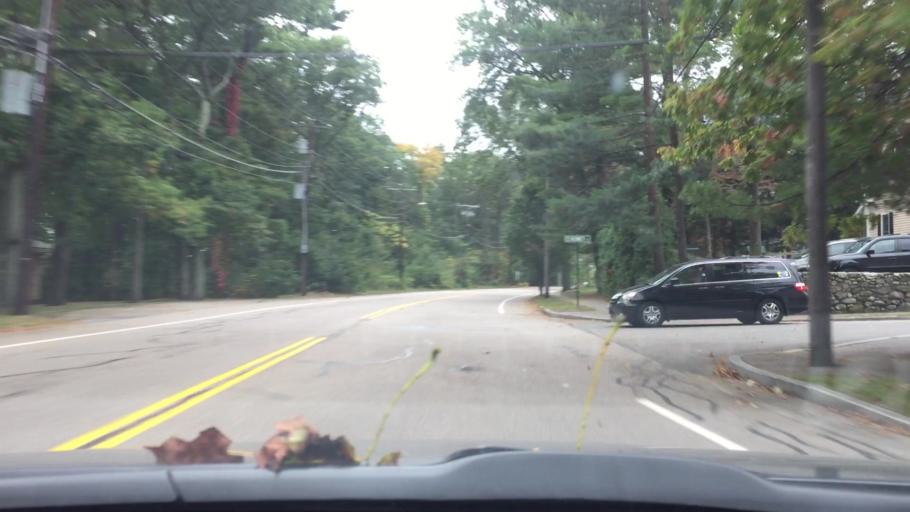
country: US
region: Massachusetts
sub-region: Norfolk County
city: Needham
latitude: 42.2810
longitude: -71.2046
